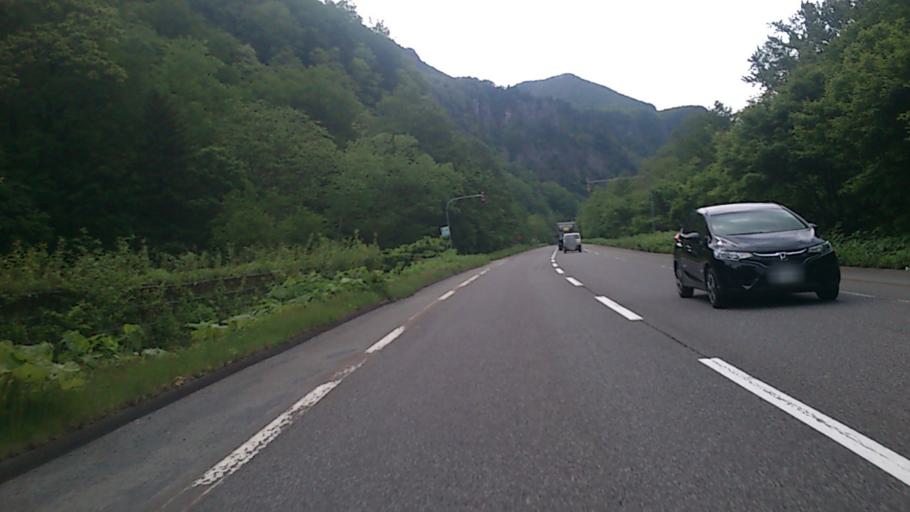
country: JP
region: Hokkaido
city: Kamikawa
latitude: 43.7563
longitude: 142.9257
